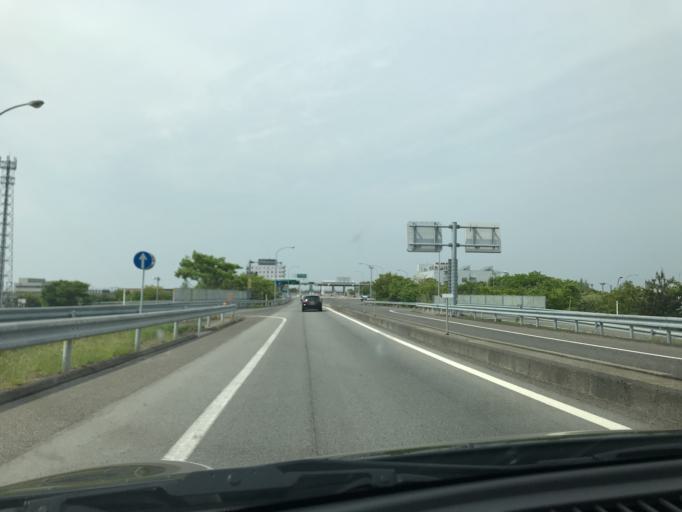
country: JP
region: Niigata
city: Kameda-honcho
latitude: 37.8790
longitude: 139.0816
